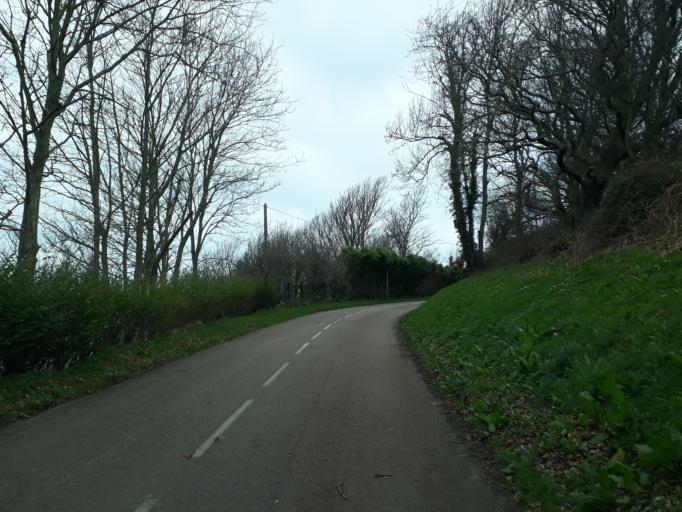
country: FR
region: Haute-Normandie
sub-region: Departement de la Seine-Maritime
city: Yport
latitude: 49.7364
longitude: 0.2929
